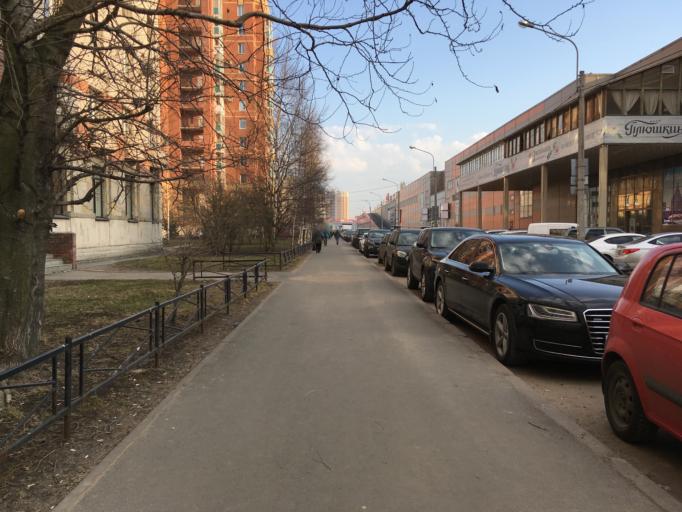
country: RU
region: St.-Petersburg
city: Komendantsky aerodrom
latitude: 60.0054
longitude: 30.2631
